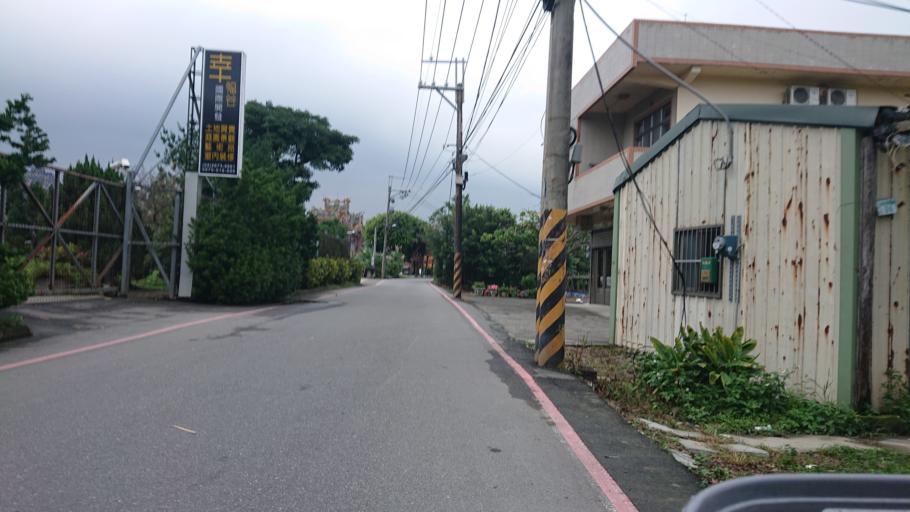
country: TW
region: Taiwan
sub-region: Taoyuan
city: Taoyuan
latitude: 24.9405
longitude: 121.3848
